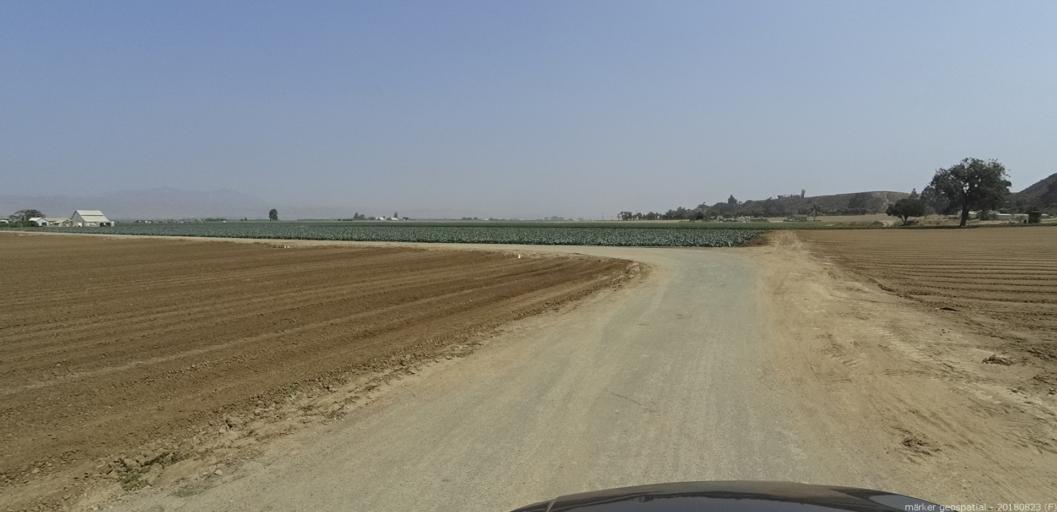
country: US
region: California
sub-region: Monterey County
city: Soledad
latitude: 36.3857
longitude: -121.3570
